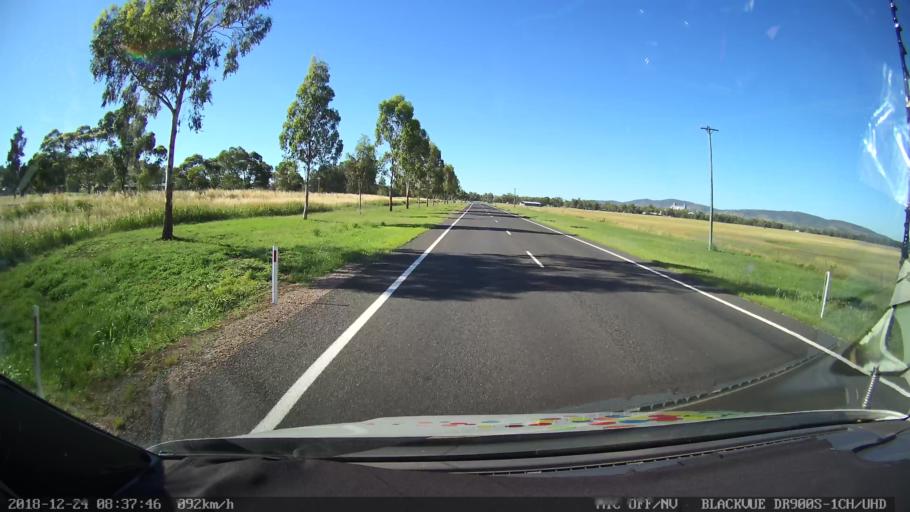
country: AU
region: New South Wales
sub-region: Liverpool Plains
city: Quirindi
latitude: -31.3336
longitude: 150.6482
